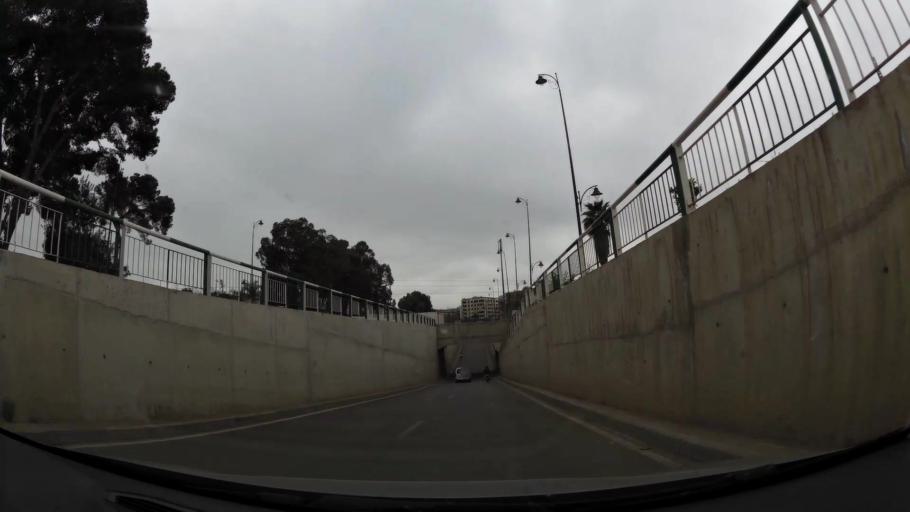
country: MA
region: Fes-Boulemane
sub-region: Fes
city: Fes
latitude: 34.0496
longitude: -5.0019
